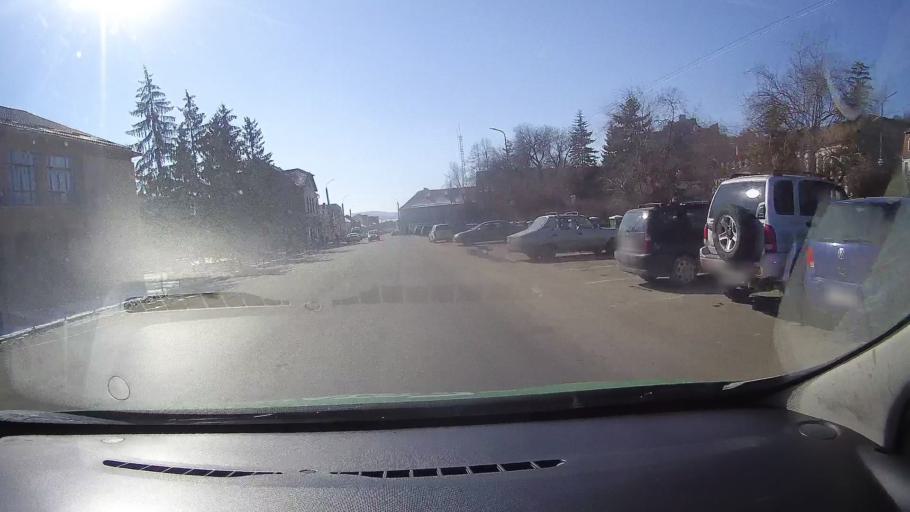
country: RO
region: Brasov
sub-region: Oras Rupea
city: Rupea
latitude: 46.0383
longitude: 25.2210
